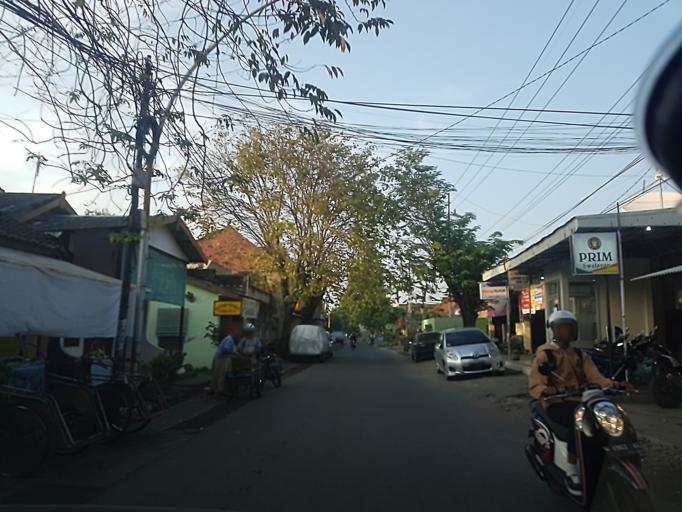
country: ID
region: East Java
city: Gresik
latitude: -7.1553
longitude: 112.6582
